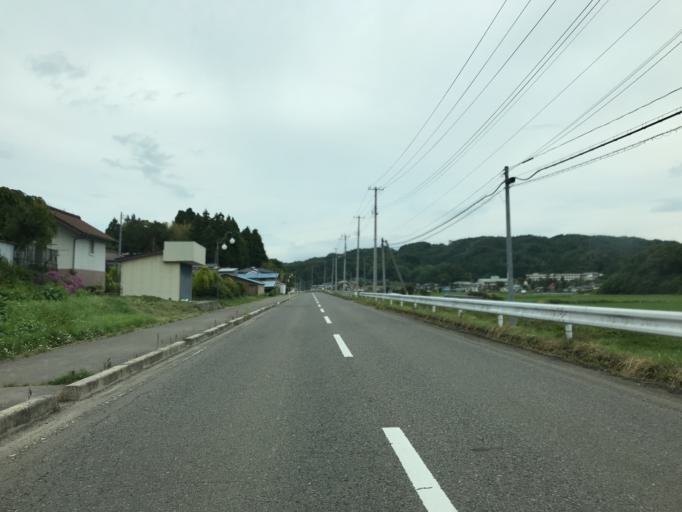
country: JP
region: Fukushima
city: Funehikimachi-funehiki
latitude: 37.3924
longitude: 140.5637
